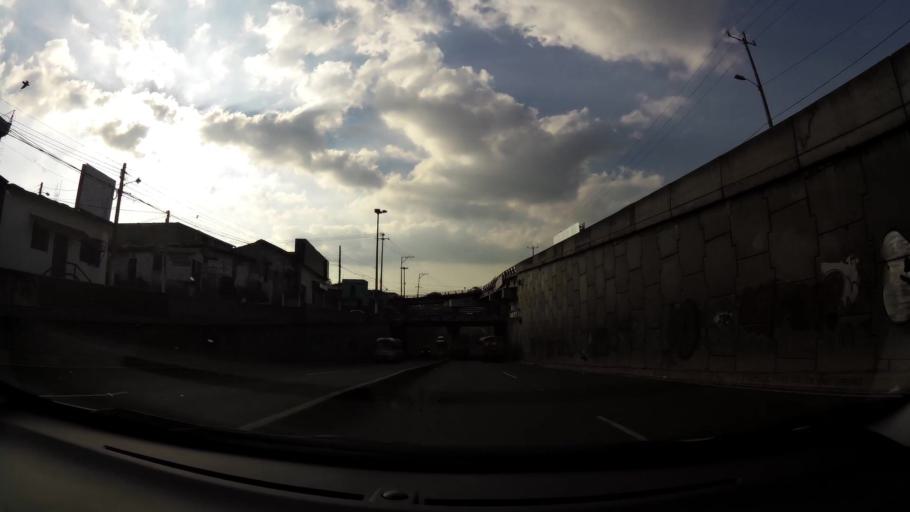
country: SV
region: San Salvador
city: San Salvador
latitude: 13.6915
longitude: -89.2164
